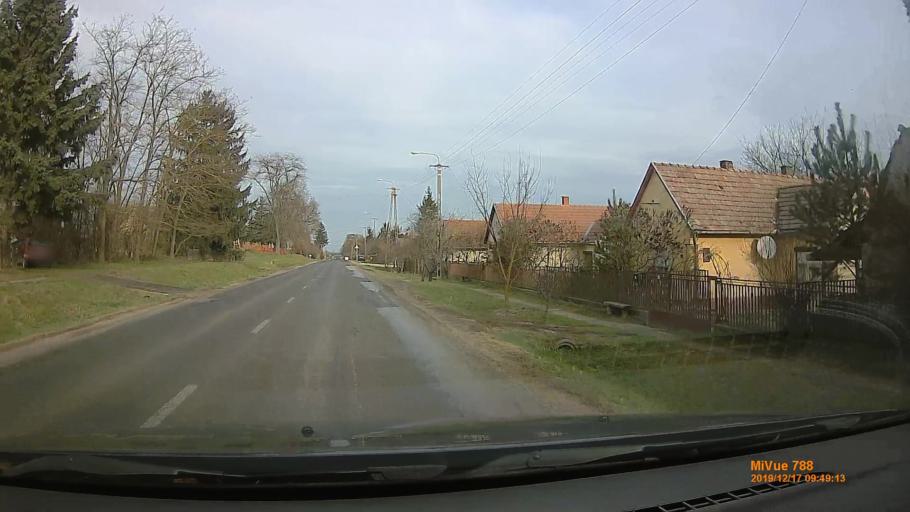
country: HU
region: Somogy
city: Karad
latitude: 46.5990
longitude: 17.8006
